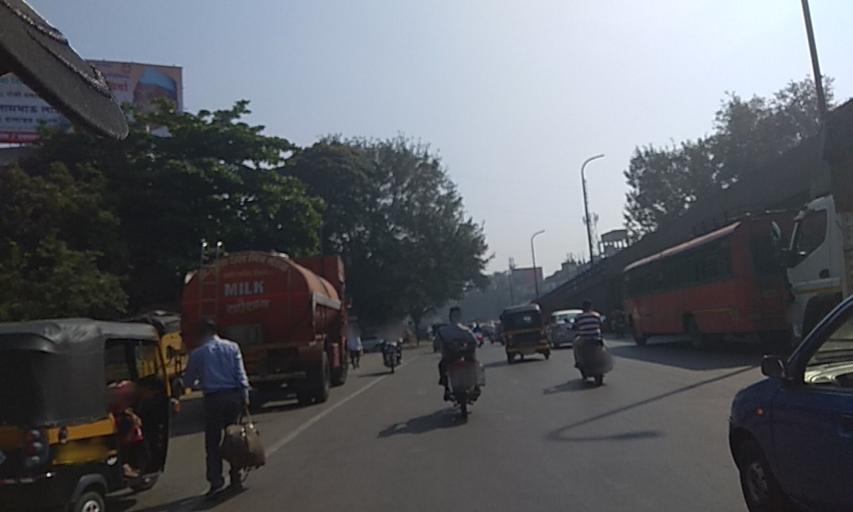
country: IN
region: Maharashtra
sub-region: Pune Division
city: Pune
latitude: 18.5023
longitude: 73.9283
